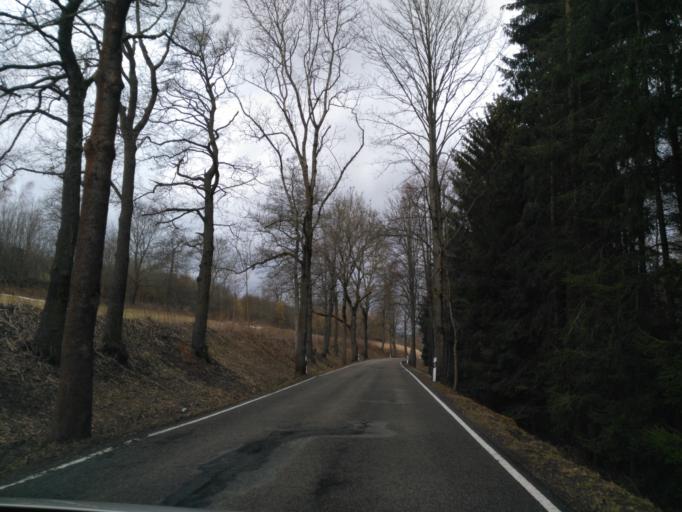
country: DE
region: Saxony
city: Konigswalde
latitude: 50.5782
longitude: 13.0521
